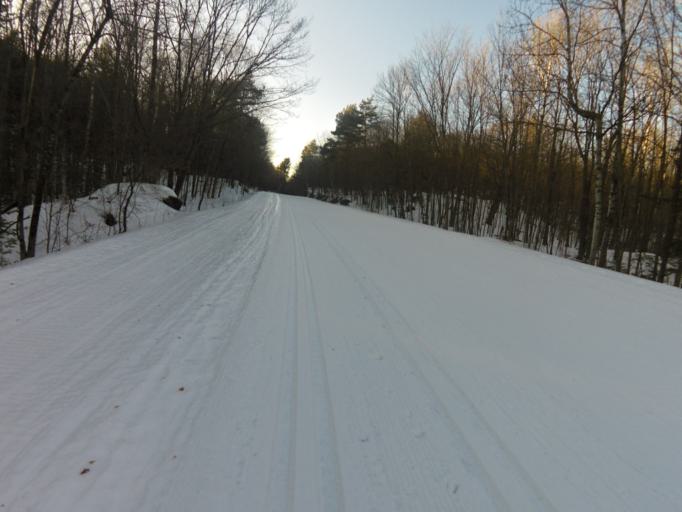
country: CA
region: Quebec
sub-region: Outaouais
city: Gatineau
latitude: 45.5153
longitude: -75.8246
